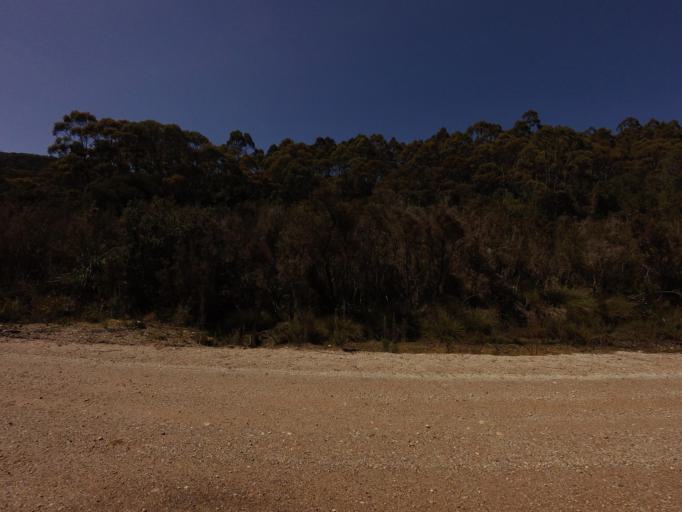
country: AU
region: Tasmania
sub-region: Huon Valley
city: Geeveston
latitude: -42.9938
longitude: 146.3712
